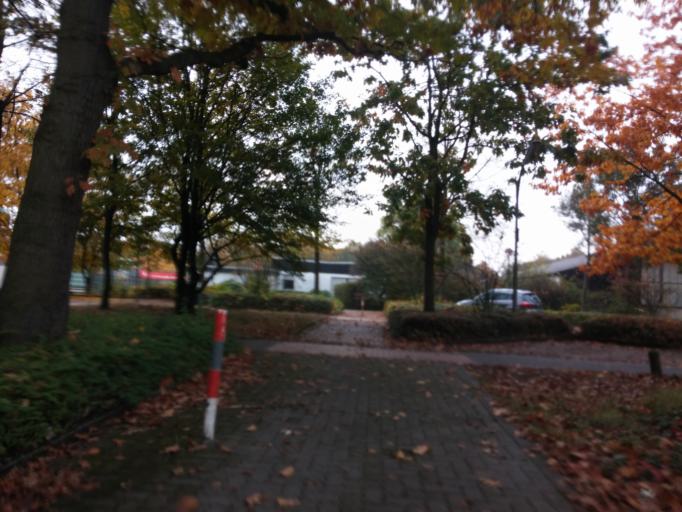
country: DE
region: North Rhine-Westphalia
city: Dorsten
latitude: 51.6659
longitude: 6.9618
